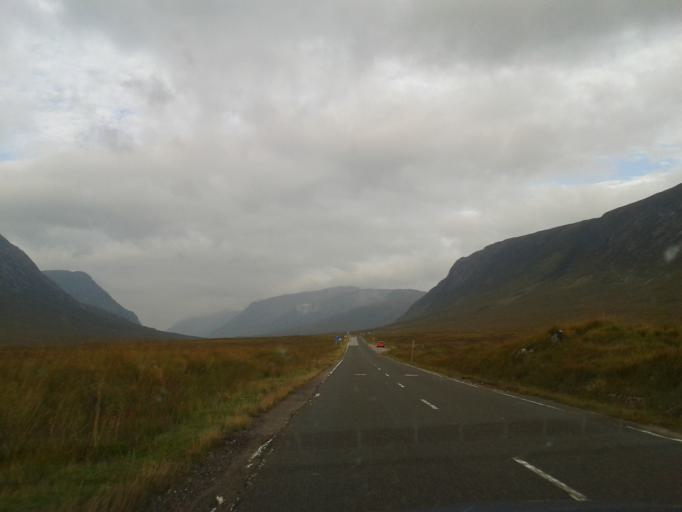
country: GB
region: Scotland
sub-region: Highland
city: Spean Bridge
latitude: 56.6525
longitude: -4.8557
